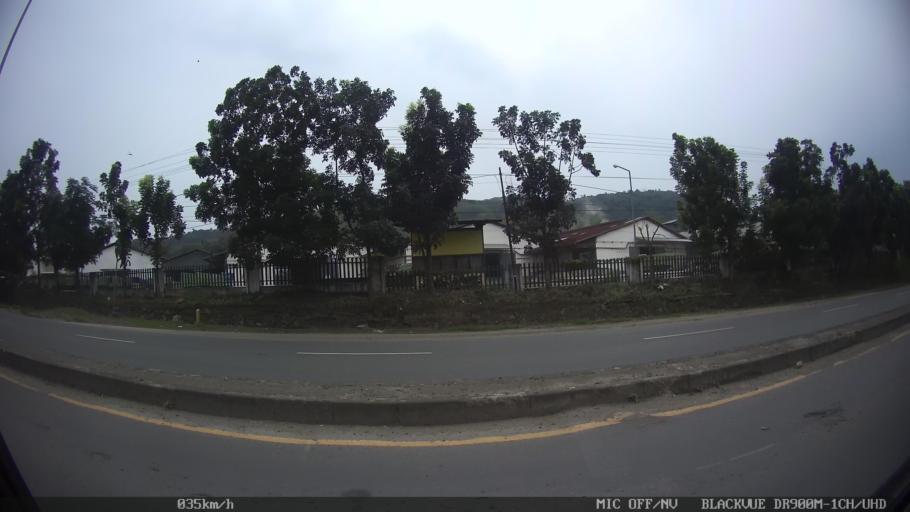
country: ID
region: Lampung
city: Bandarlampung
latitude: -5.4326
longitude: 105.2975
